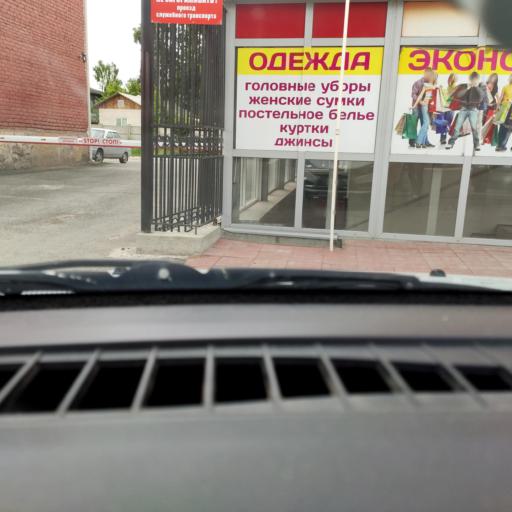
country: RU
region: Perm
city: Kungur
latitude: 57.4258
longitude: 56.9508
